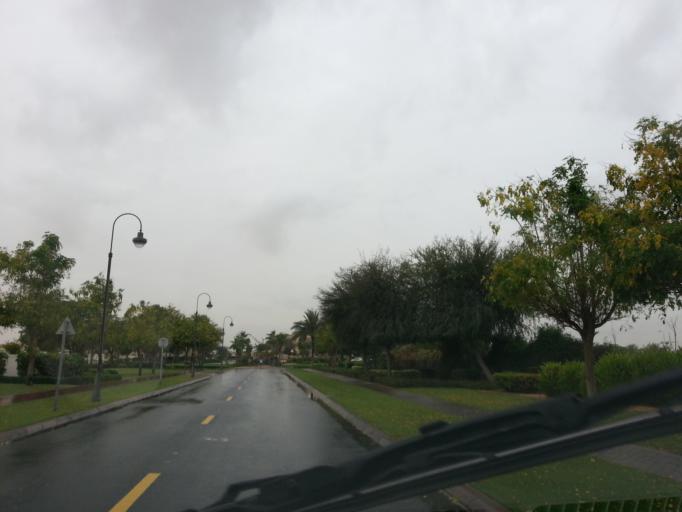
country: AE
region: Dubai
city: Dubai
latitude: 25.0348
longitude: 55.2095
